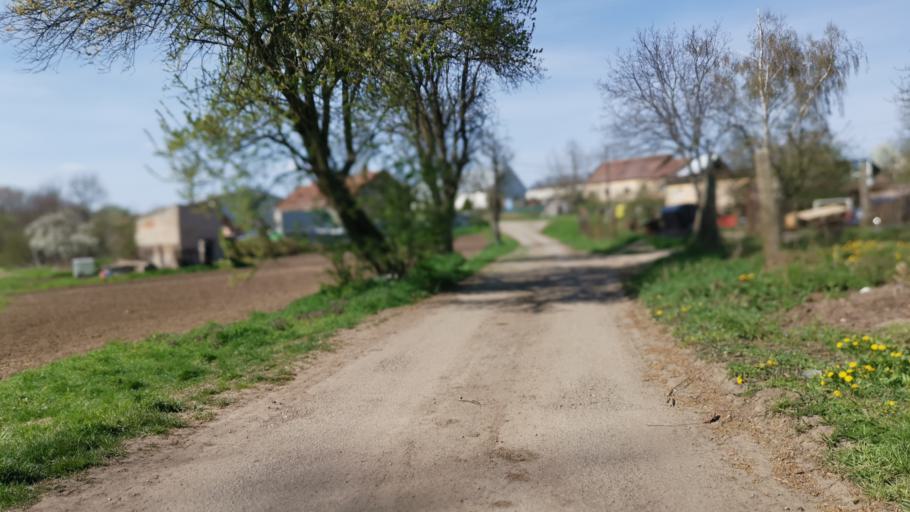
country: SK
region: Trnavsky
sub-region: Okres Skalica
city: Holic
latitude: 48.7654
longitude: 17.1890
